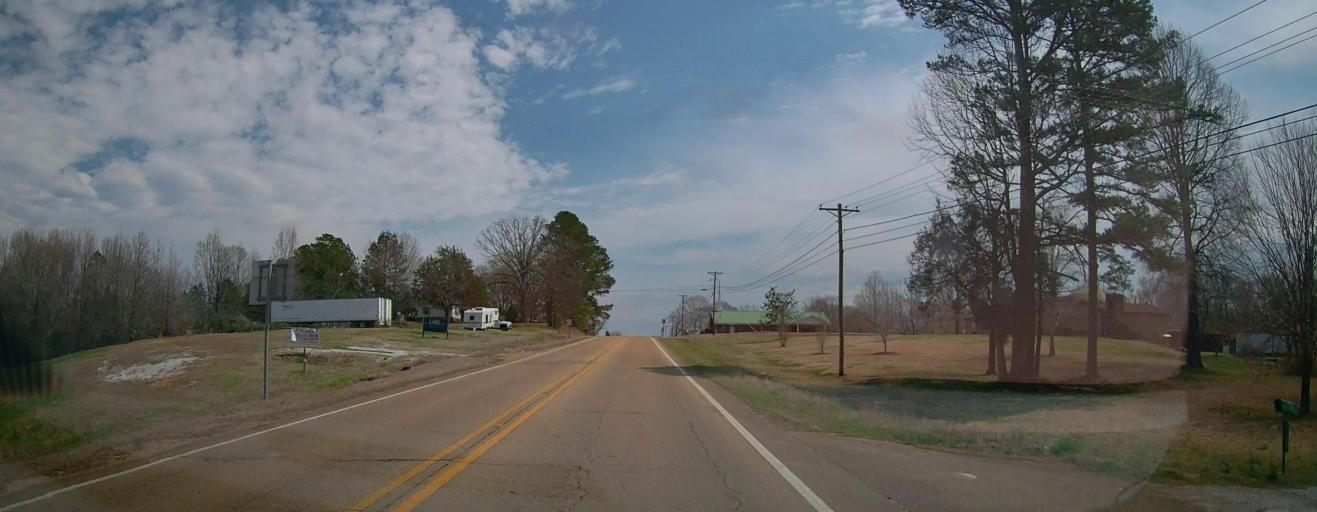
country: US
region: Mississippi
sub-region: Benton County
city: Ashland
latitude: 34.6180
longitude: -89.1940
